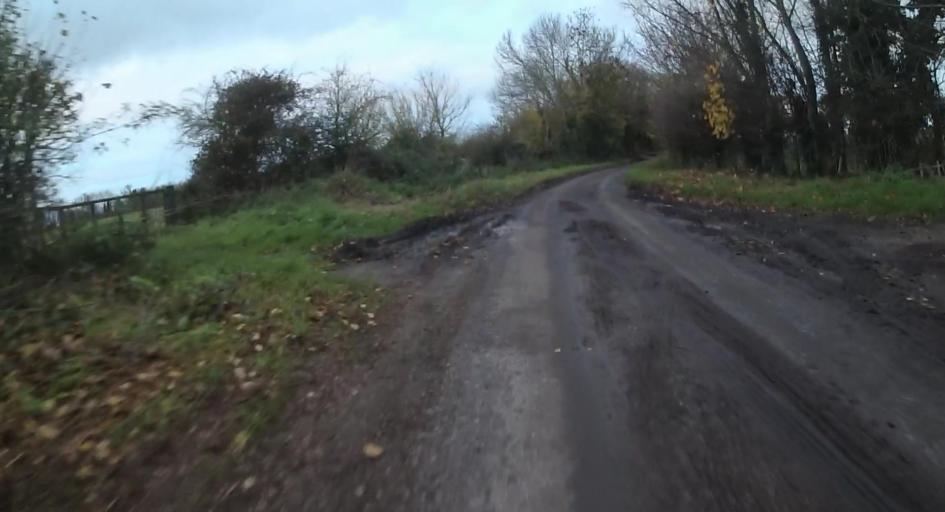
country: GB
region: England
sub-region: Hampshire
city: Long Sutton
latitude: 51.2136
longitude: -0.9437
